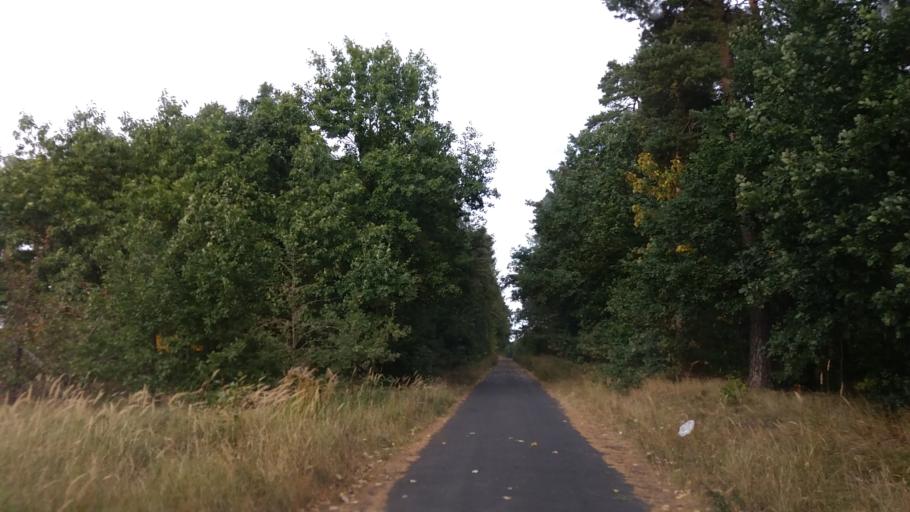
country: PL
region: Lubusz
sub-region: Powiat strzelecko-drezdenecki
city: Strzelce Krajenskie
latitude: 52.9597
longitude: 15.4543
